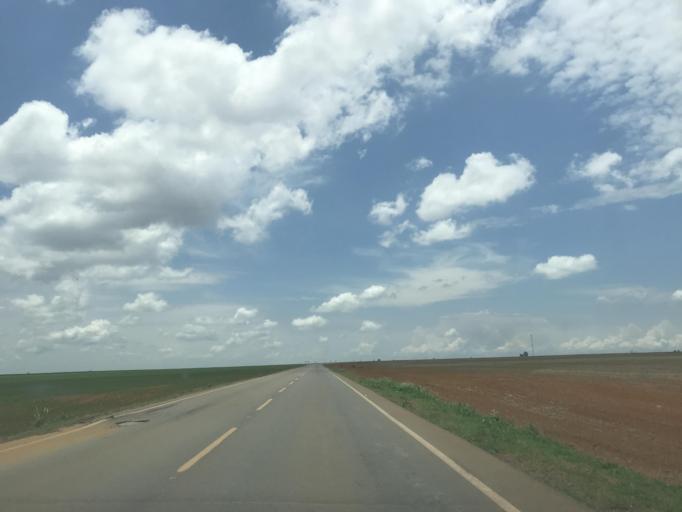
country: BR
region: Goias
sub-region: Vianopolis
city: Vianopolis
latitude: -16.5229
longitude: -48.2388
